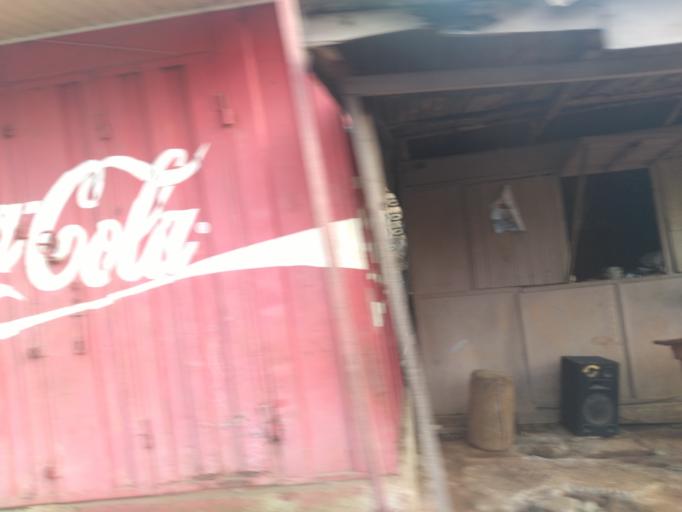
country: GH
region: Ashanti
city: Kumasi
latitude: 6.6771
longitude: -1.5912
